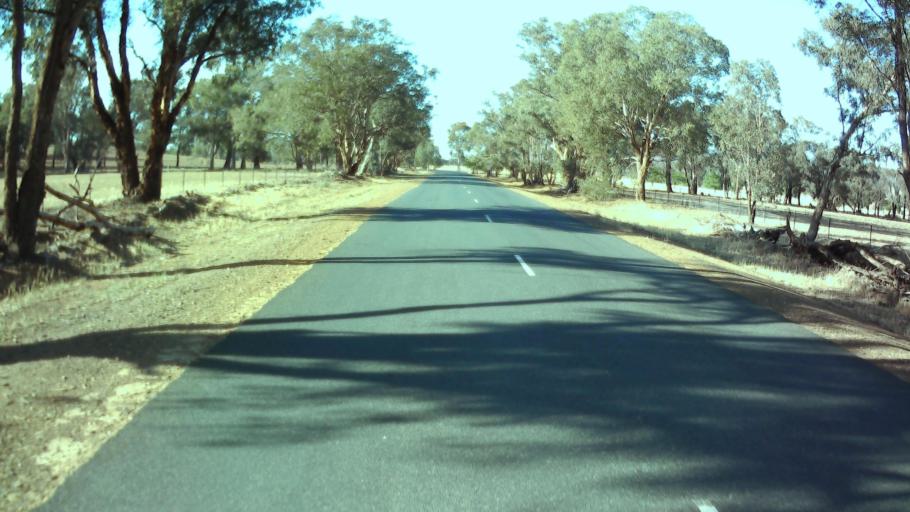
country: AU
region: New South Wales
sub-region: Weddin
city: Grenfell
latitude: -33.9406
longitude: 148.1365
